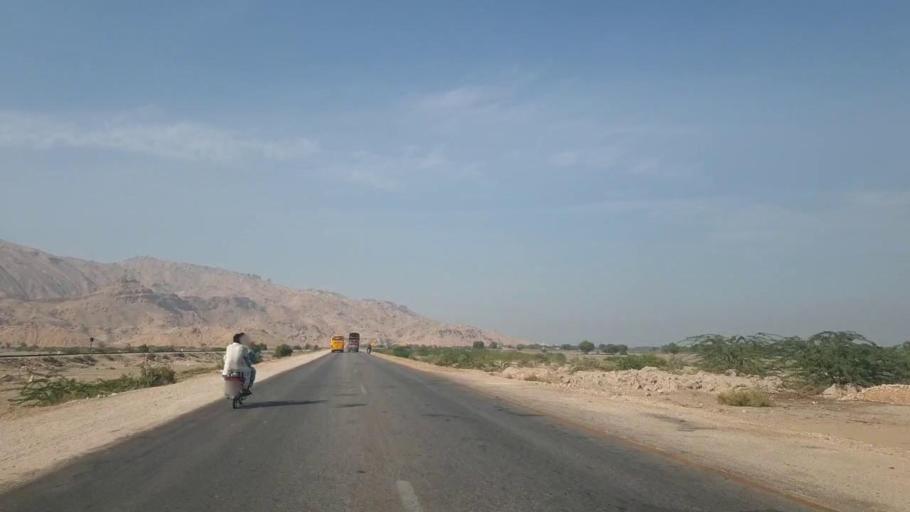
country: PK
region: Sindh
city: Sehwan
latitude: 26.2778
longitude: 67.8978
